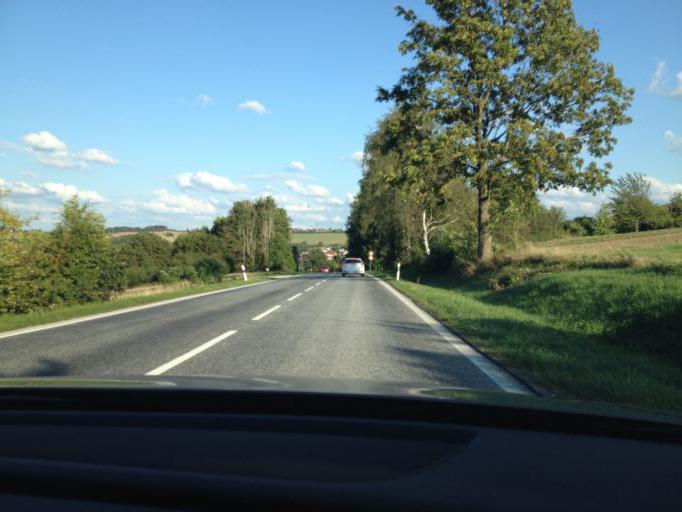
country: DE
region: Saarland
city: Tholey
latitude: 49.4755
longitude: 7.0547
